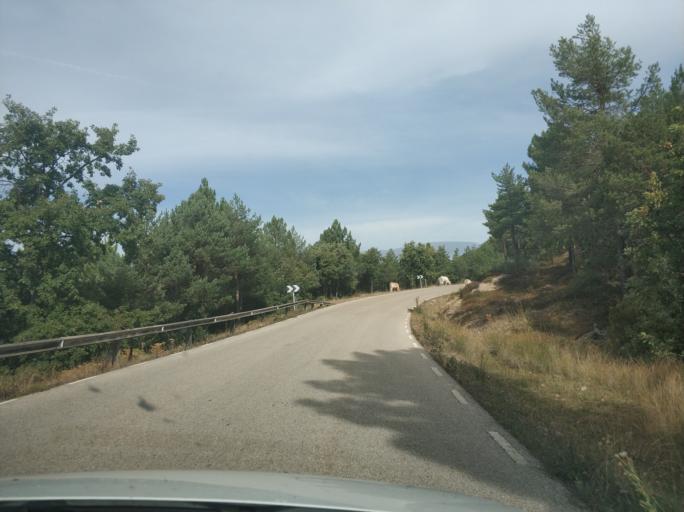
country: ES
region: Castille and Leon
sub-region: Provincia de Soria
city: Duruelo de la Sierra
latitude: 41.9019
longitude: -2.9414
